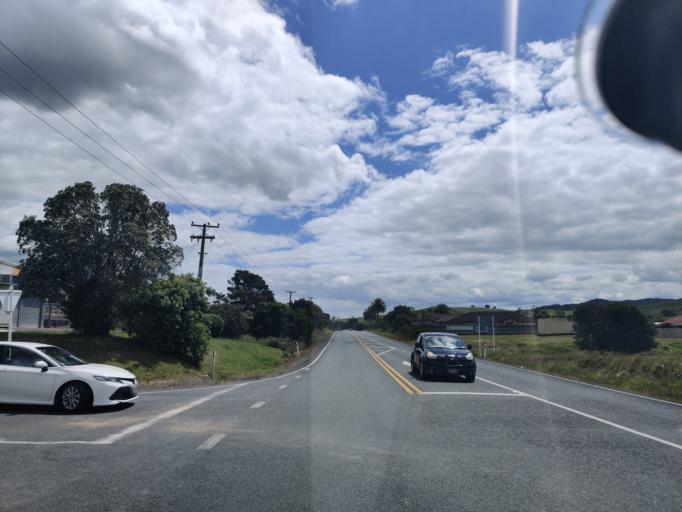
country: NZ
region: Northland
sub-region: Far North District
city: Paihia
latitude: -35.2810
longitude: 174.0467
